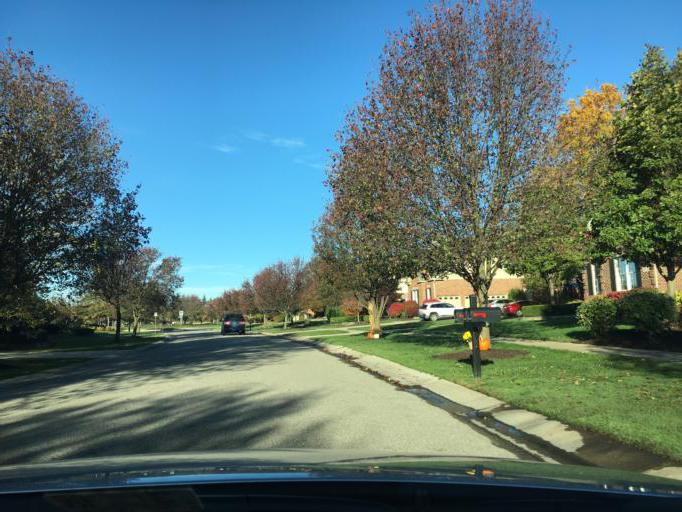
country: US
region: Michigan
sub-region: Wayne County
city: Northville
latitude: 42.4012
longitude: -83.4926
